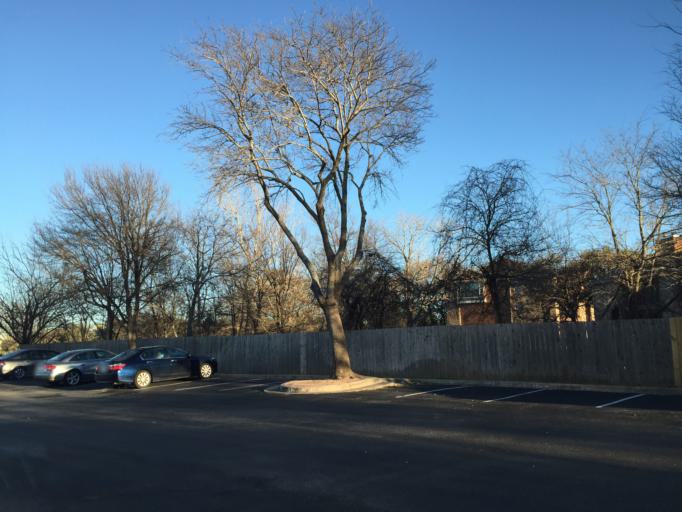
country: US
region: Texas
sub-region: Williamson County
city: Jollyville
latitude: 30.4356
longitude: -97.7755
